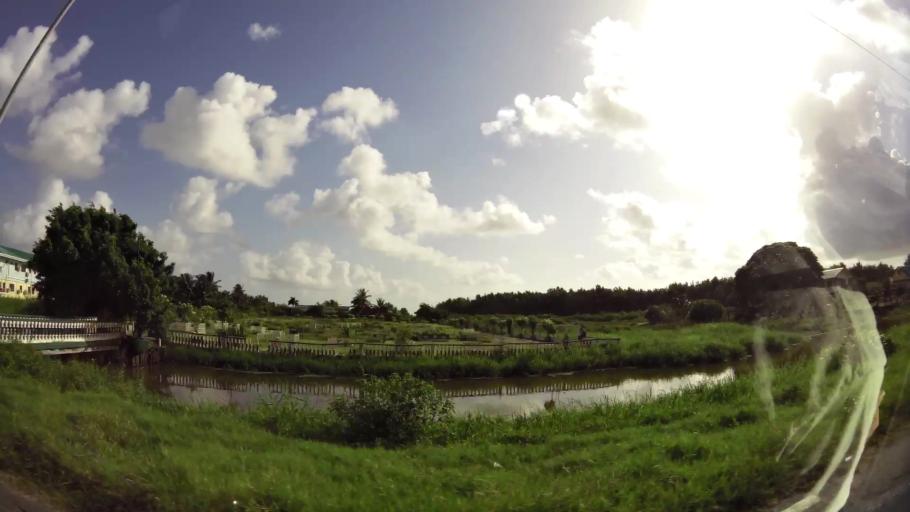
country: GY
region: Demerara-Mahaica
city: Georgetown
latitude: 6.8086
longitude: -58.0560
